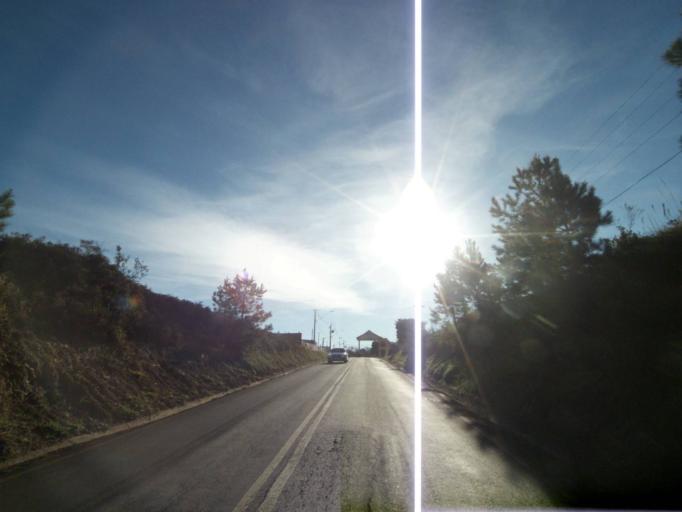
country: BR
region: Parana
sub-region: Tibagi
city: Tibagi
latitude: -24.5275
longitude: -50.3997
